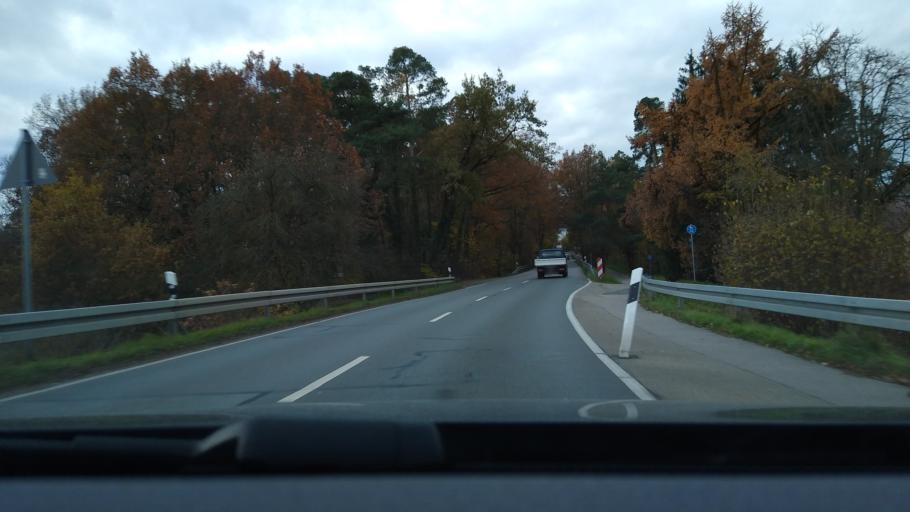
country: DE
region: Bavaria
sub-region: Regierungsbezirk Mittelfranken
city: Schwabach
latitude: 49.3463
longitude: 11.0505
